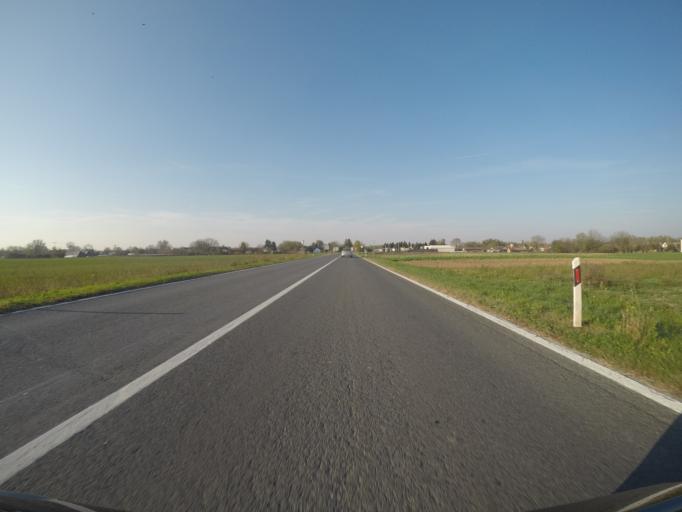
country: HU
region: Somogy
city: Barcs
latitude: 45.9378
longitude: 17.4609
